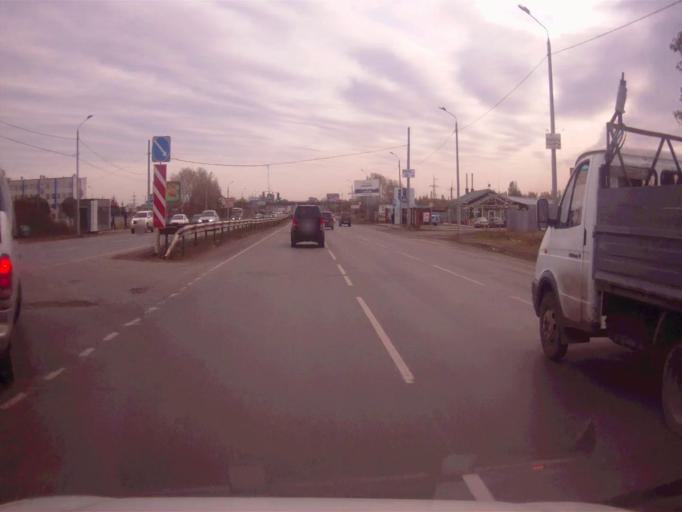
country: RU
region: Chelyabinsk
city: Novosineglazovskiy
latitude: 55.0652
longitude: 61.3966
